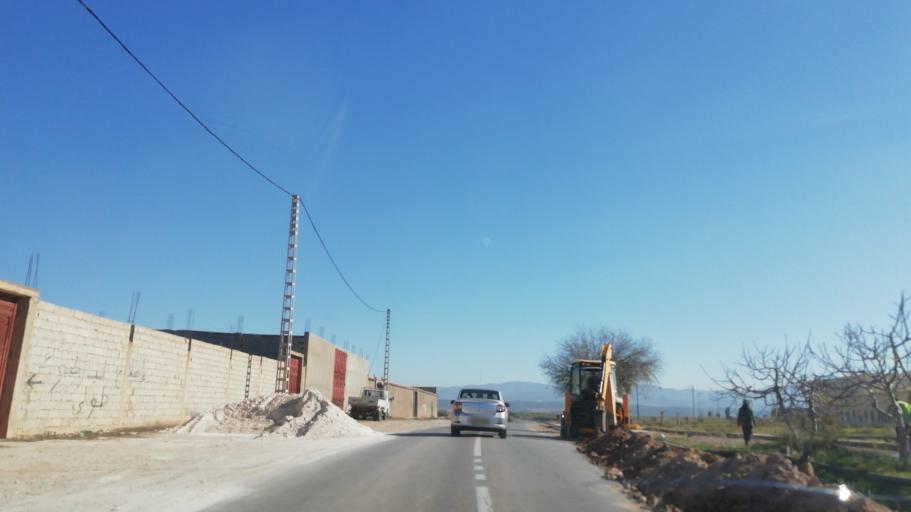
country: DZ
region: Tlemcen
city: Nedroma
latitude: 34.8335
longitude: -1.6826
